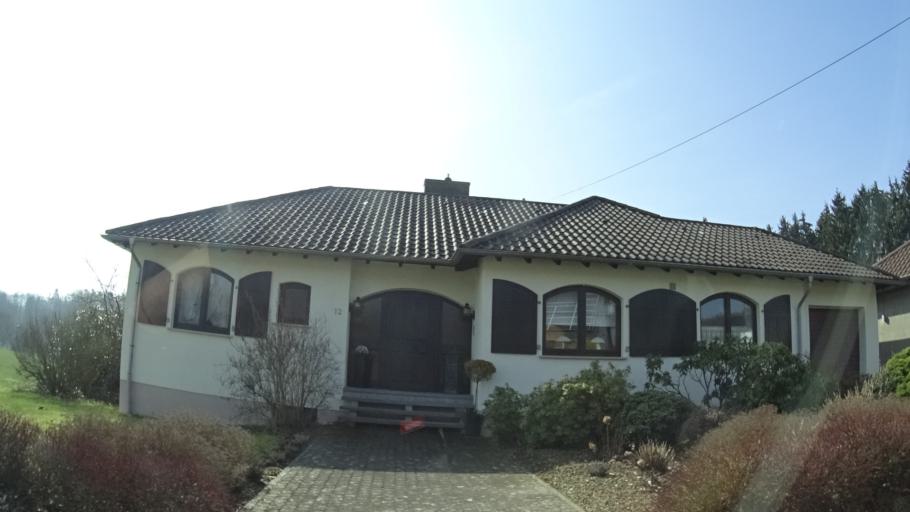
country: DE
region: Saarland
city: Nohfelden
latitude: 49.5857
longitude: 7.1213
